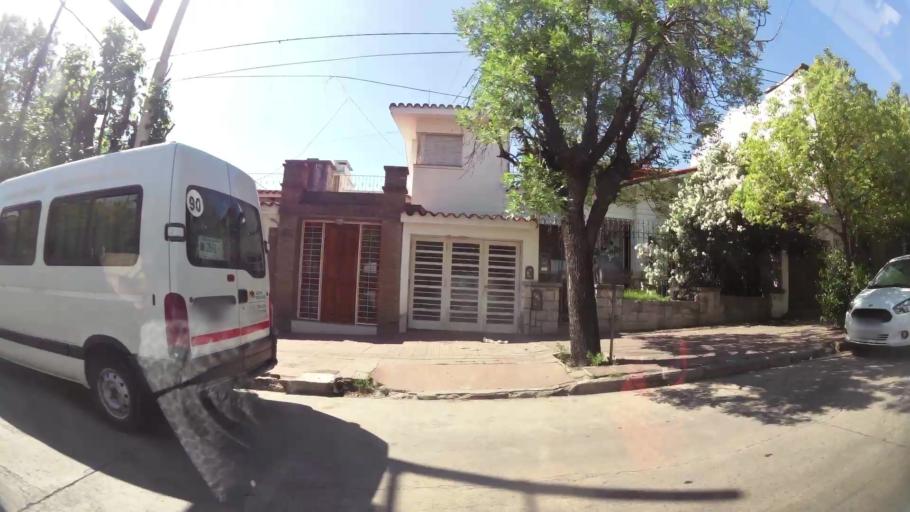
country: AR
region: Cordoba
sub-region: Departamento de Capital
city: Cordoba
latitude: -31.4092
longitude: -64.1621
